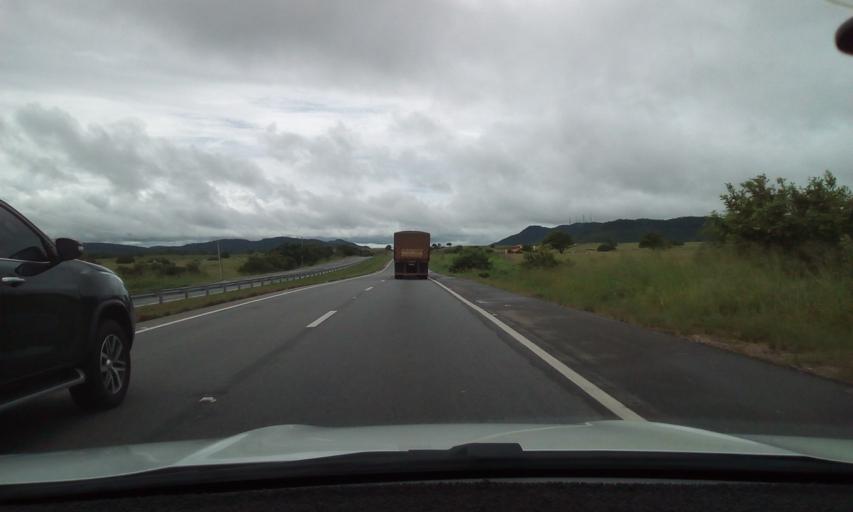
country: BR
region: Paraiba
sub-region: Gurinhem
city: Gurinhem
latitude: -7.1889
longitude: -35.4620
